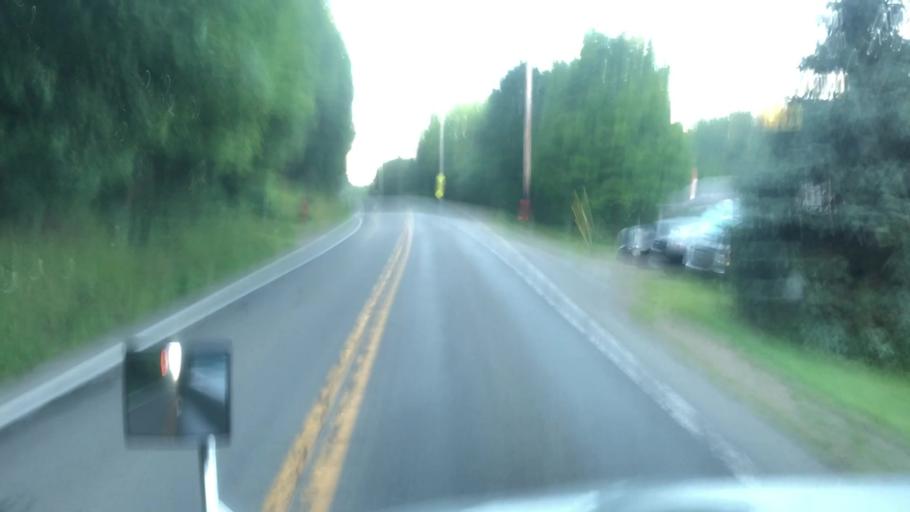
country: US
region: Pennsylvania
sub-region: Venango County
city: Hasson Heights
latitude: 41.4948
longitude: -79.6464
